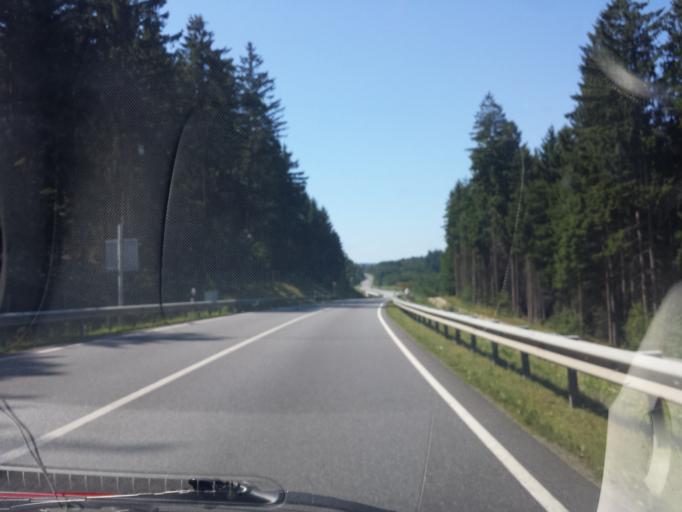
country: DE
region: Bavaria
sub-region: Upper Palatinate
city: Furth im Wald
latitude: 49.2923
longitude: 12.8359
